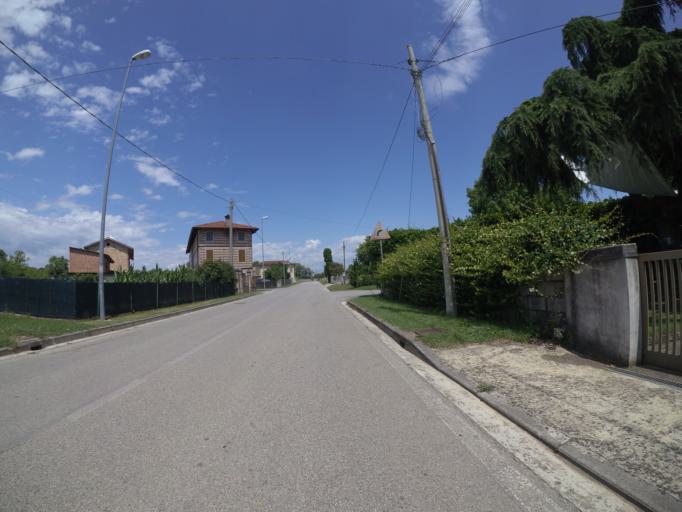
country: IT
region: Friuli Venezia Giulia
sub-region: Provincia di Udine
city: Lestizza
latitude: 45.9675
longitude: 13.1171
